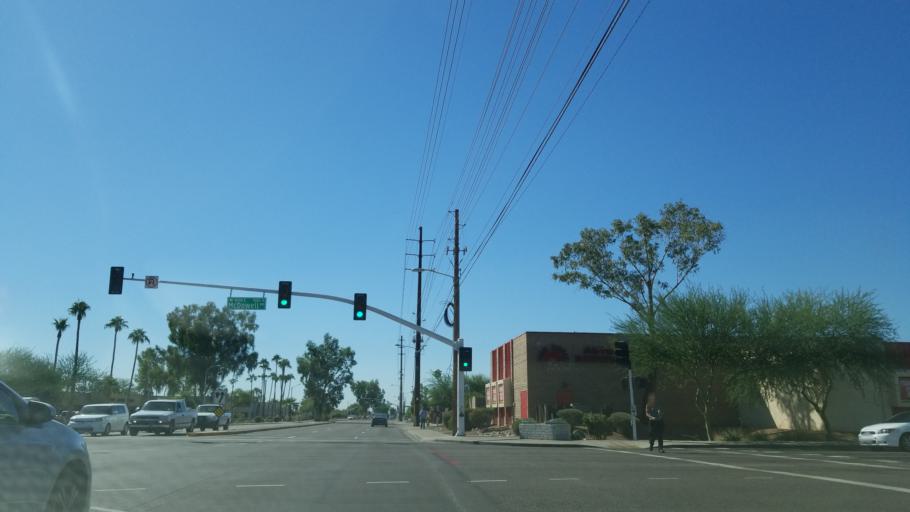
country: US
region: Arizona
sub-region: Maricopa County
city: Tempe
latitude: 33.4600
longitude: -111.9091
